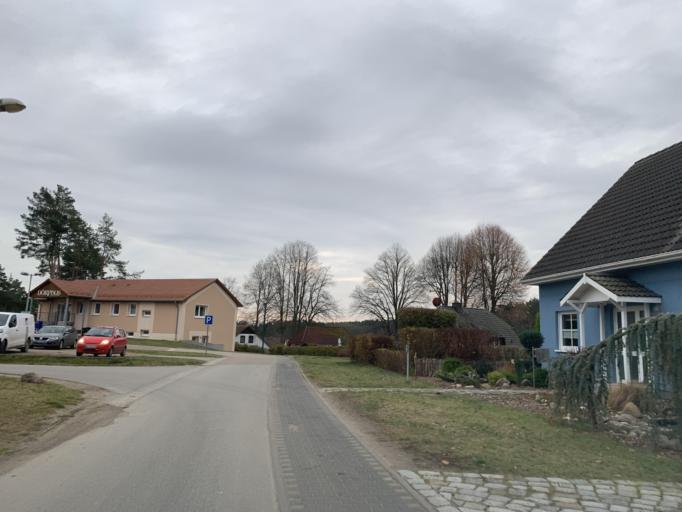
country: DE
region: Mecklenburg-Vorpommern
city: Blankensee
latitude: 53.4038
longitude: 13.2689
